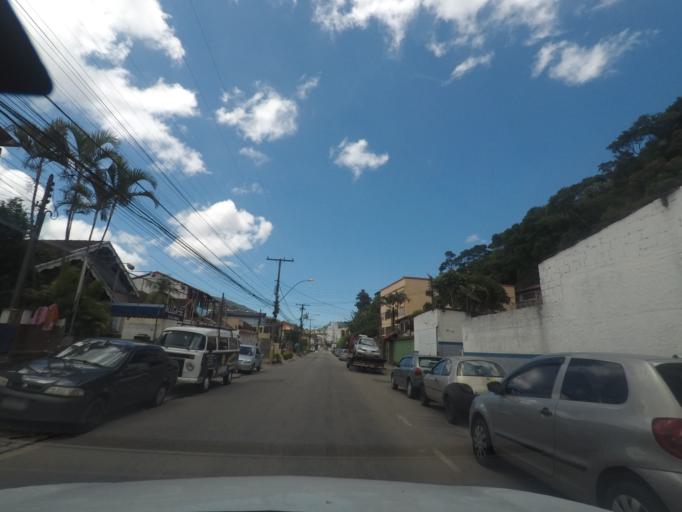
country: BR
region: Rio de Janeiro
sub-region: Teresopolis
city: Teresopolis
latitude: -22.4056
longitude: -42.9671
